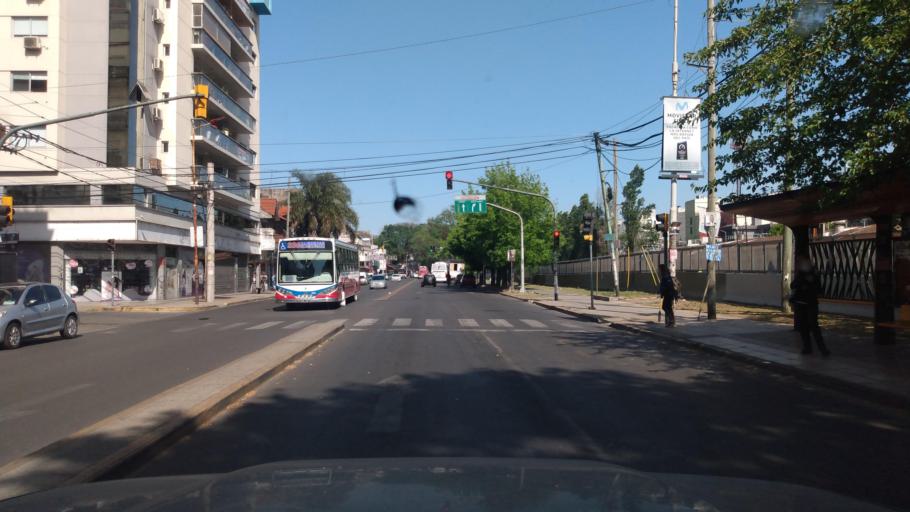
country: AR
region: Buenos Aires
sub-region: Partido de Moron
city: Moron
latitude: -34.6442
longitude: -58.5880
